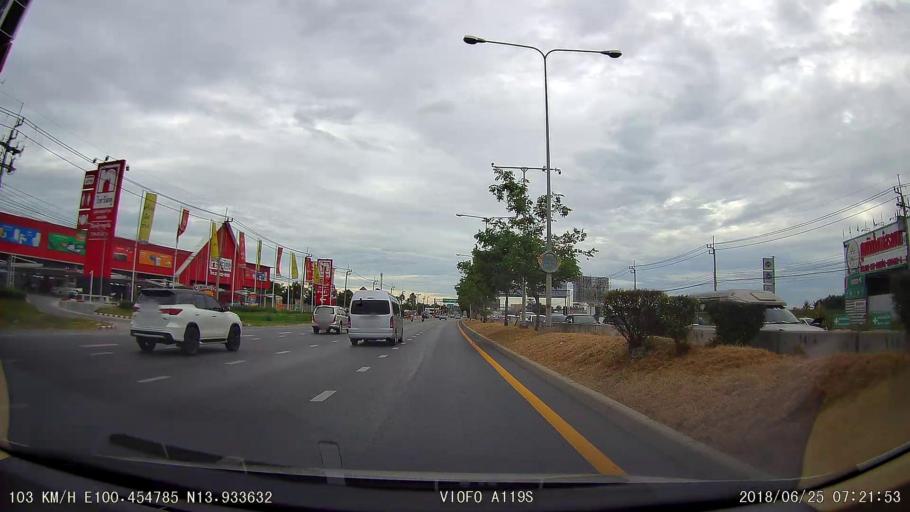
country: TH
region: Nonthaburi
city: Bang Bua Thong
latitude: 13.9338
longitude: 100.4549
